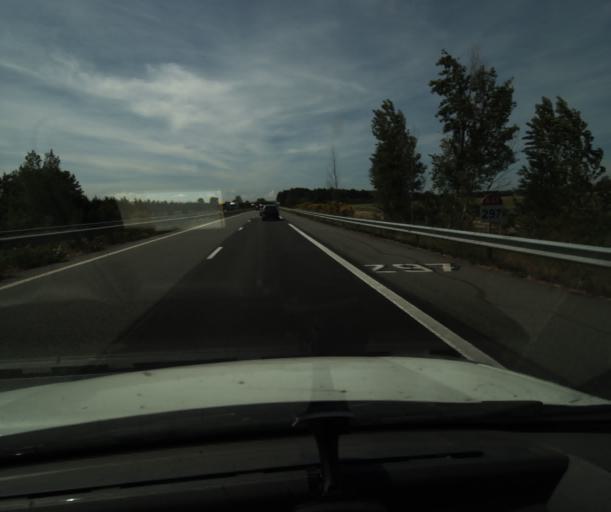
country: FR
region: Languedoc-Roussillon
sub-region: Departement de l'Aude
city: Villepinte
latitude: 43.2528
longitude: 2.0462
